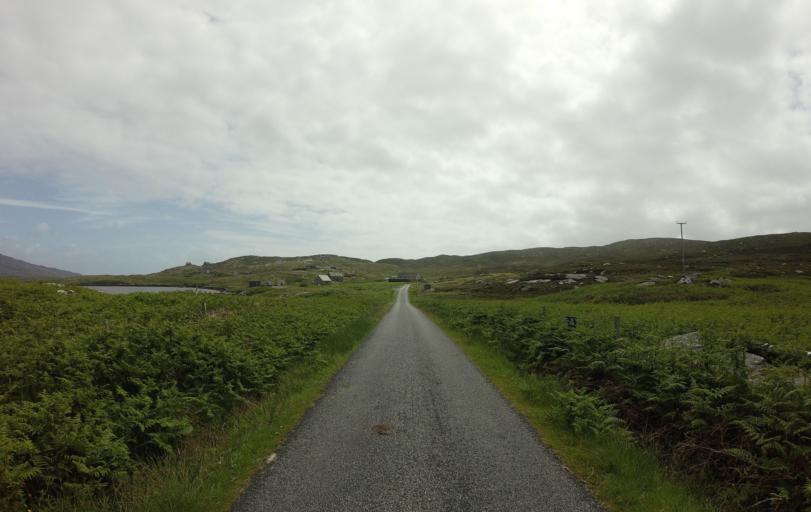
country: GB
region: Scotland
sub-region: Eilean Siar
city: Isle of South Uist
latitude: 57.1364
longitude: -7.3367
